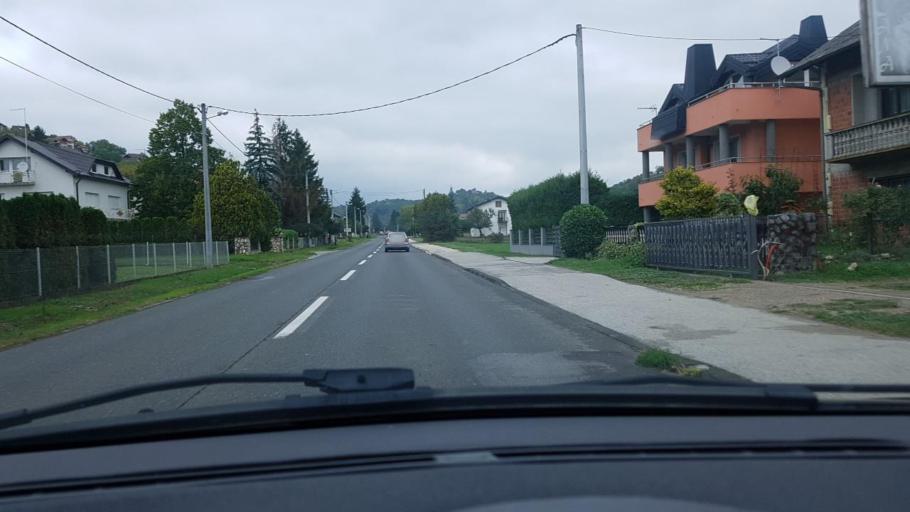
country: HR
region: Grad Zagreb
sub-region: Sesvete
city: Sesvete
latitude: 45.8800
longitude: 16.1154
